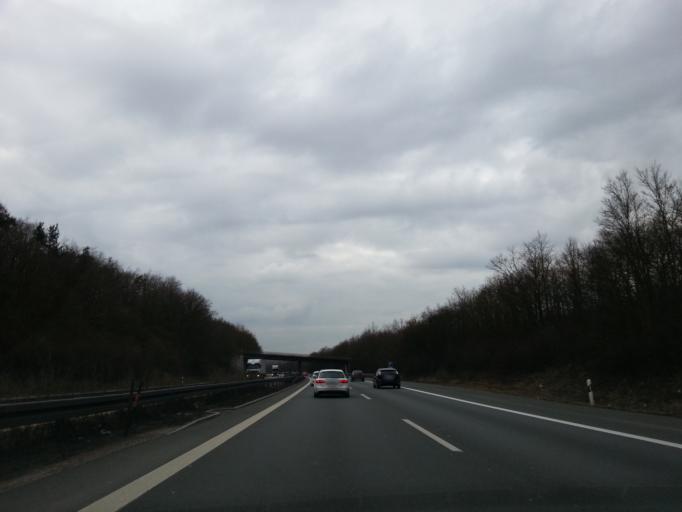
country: DE
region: Bavaria
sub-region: Regierungsbezirk Unterfranken
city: Dettelbach
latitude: 49.7871
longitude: 10.1894
